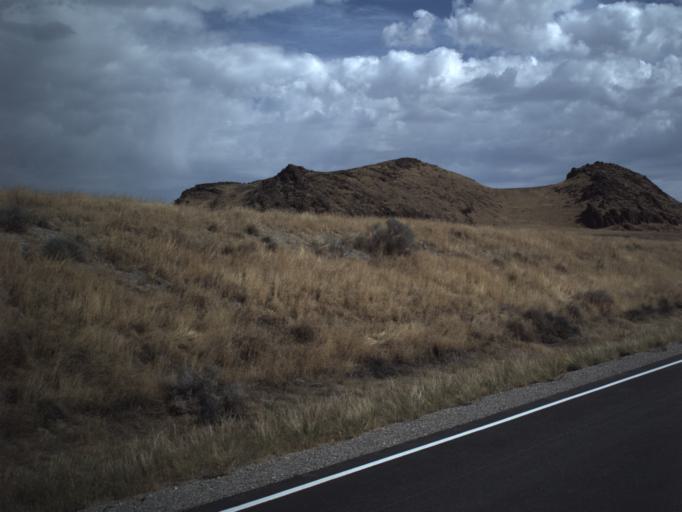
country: US
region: Utah
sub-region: Tooele County
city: Wendover
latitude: 41.3758
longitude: -114.0115
